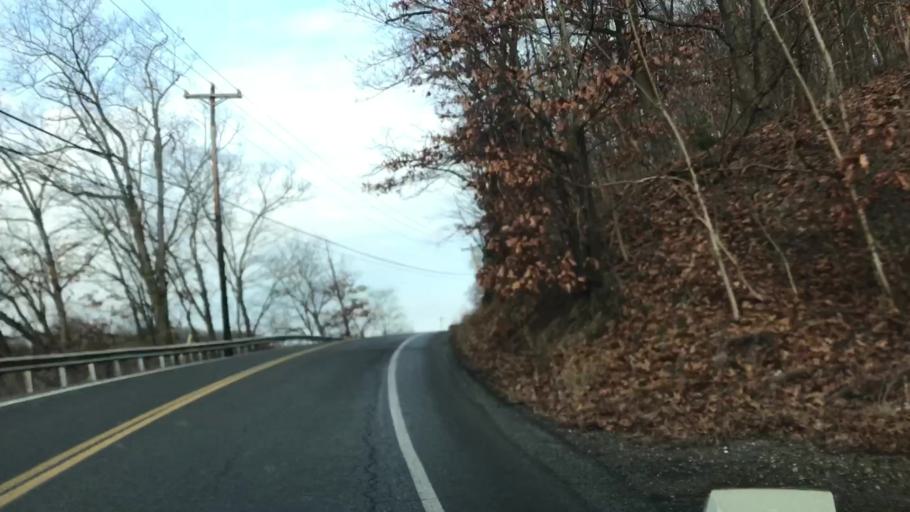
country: US
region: Pennsylvania
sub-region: Allegheny County
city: Ben Avon
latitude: 40.5413
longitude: -80.0791
